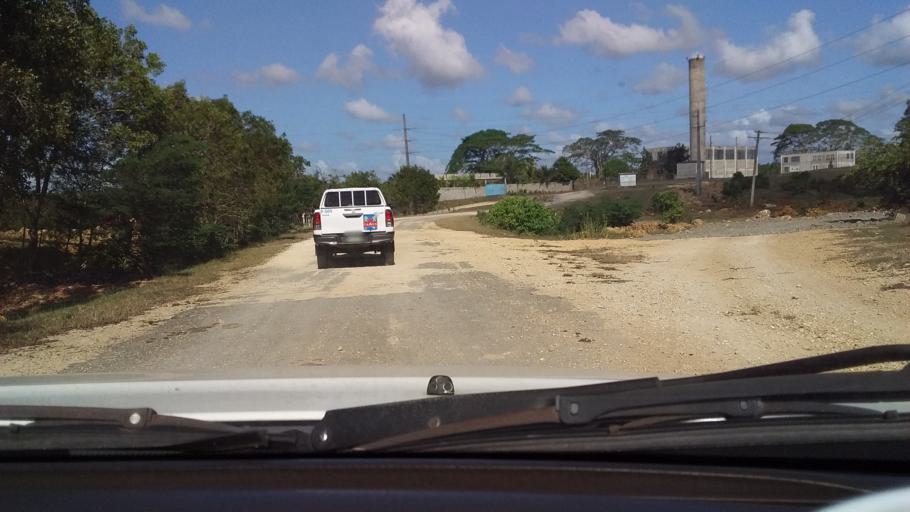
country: DO
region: Santo Domingo
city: Guerra
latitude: 18.5694
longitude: -69.7850
